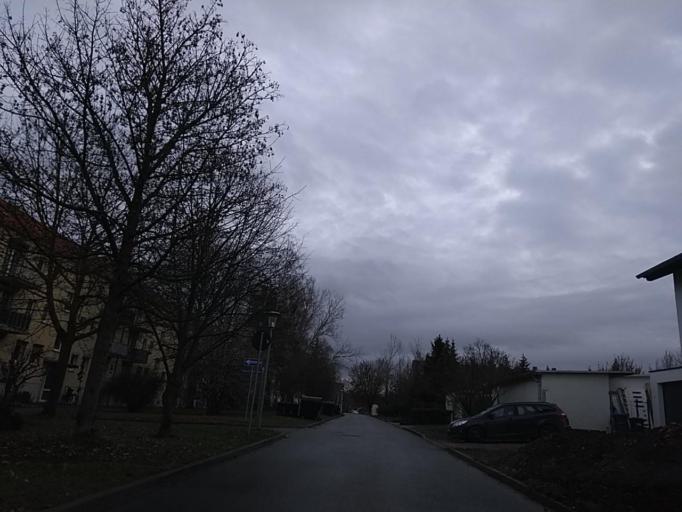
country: DE
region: Saxony-Anhalt
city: Schraplau
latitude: 51.4457
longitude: 11.6751
